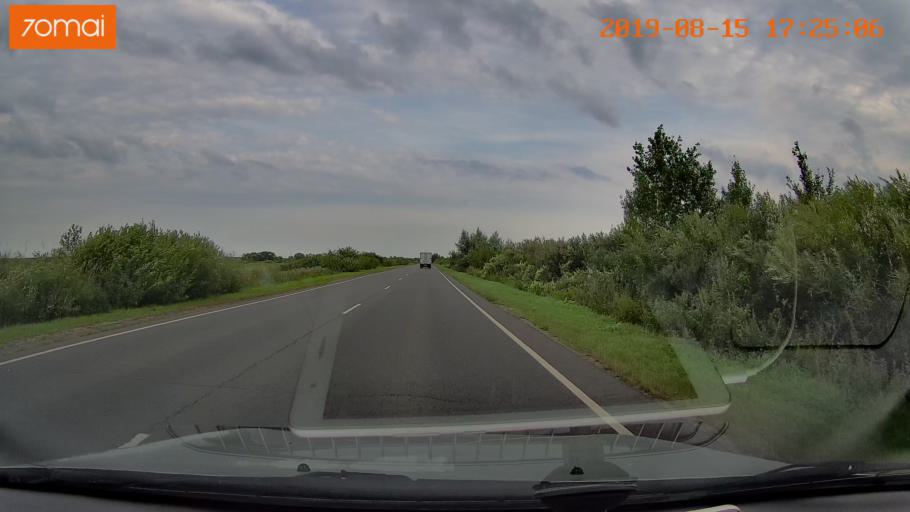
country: RU
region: Moskovskaya
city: Ashitkovo
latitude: 55.3788
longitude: 38.5618
